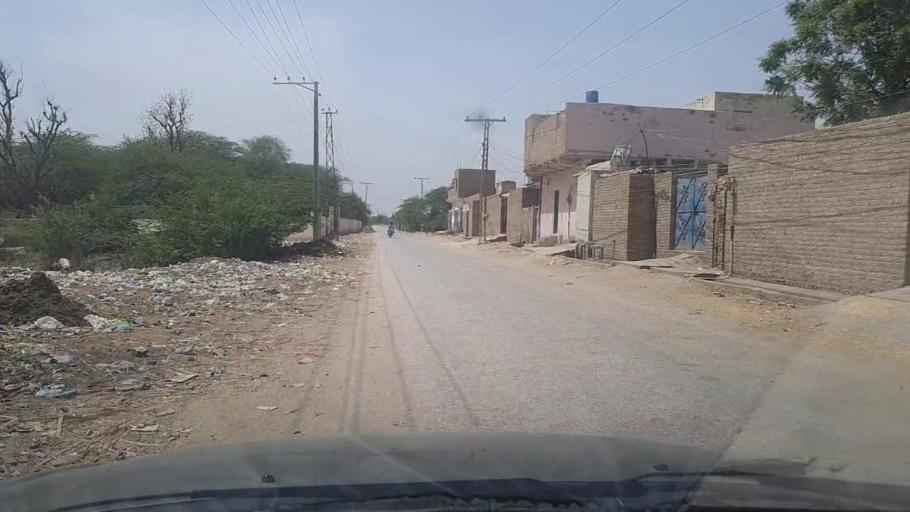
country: PK
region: Sindh
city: Bhiria
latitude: 26.9003
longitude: 68.2118
